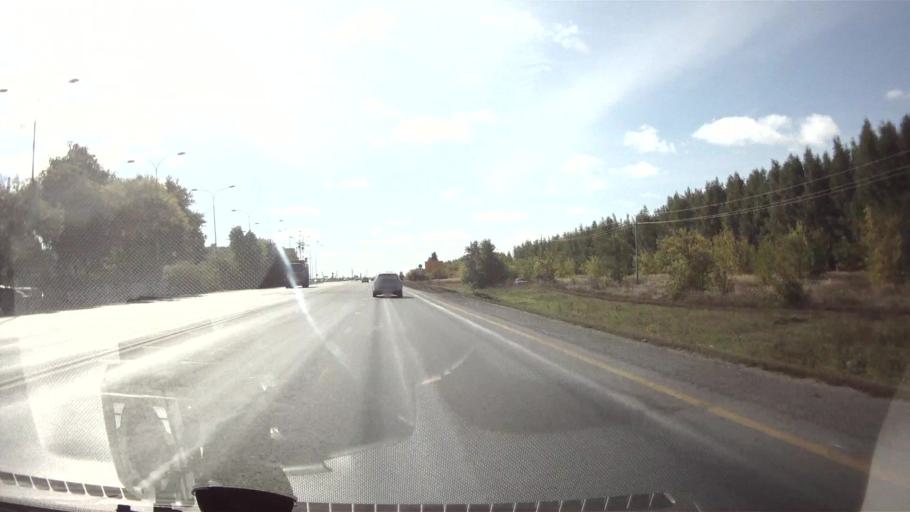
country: RU
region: Ulyanovsk
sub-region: Ulyanovskiy Rayon
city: Ulyanovsk
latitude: 54.2882
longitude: 48.2557
